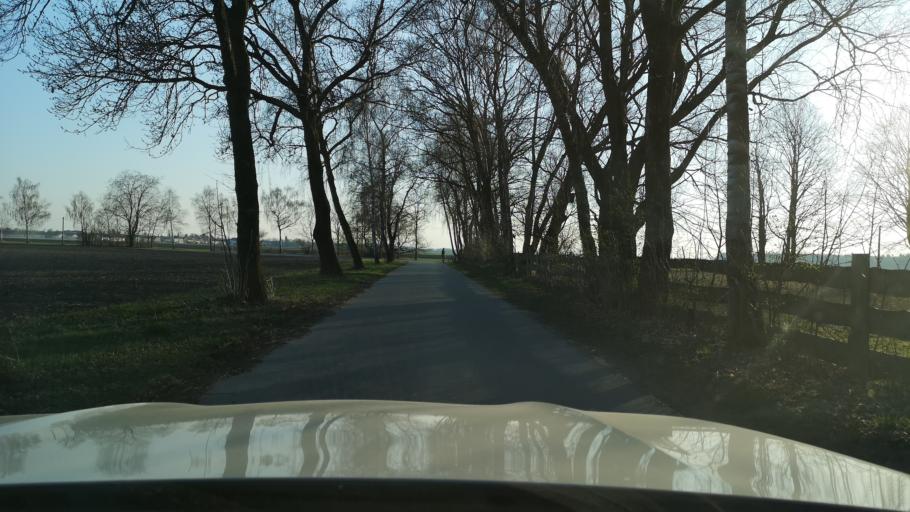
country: DE
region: Bavaria
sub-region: Upper Bavaria
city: Kirchheim bei Muenchen
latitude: 48.1882
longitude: 11.7524
